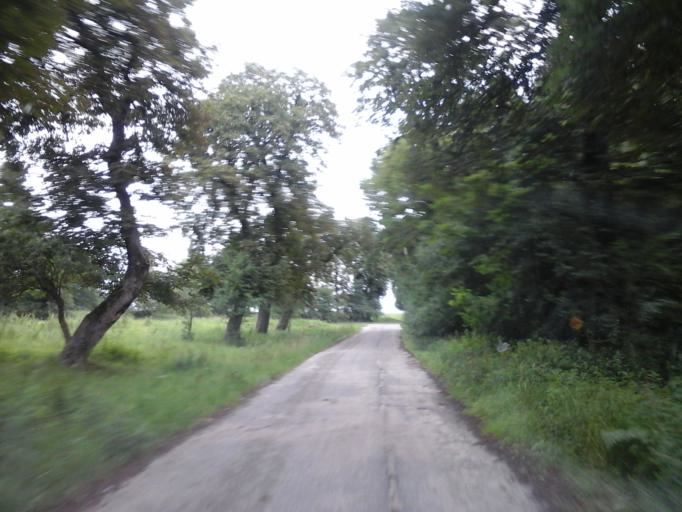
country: PL
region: West Pomeranian Voivodeship
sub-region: Powiat choszczenski
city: Krzecin
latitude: 52.9736
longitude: 15.4261
